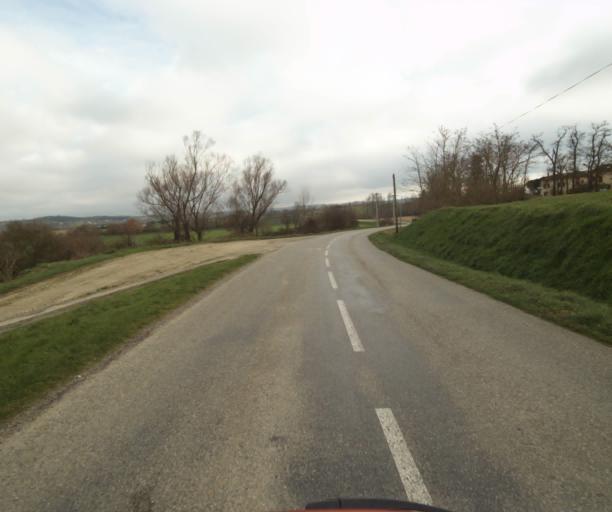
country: FR
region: Languedoc-Roussillon
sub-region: Departement de l'Aude
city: Belpech
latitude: 43.2129
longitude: 1.7251
